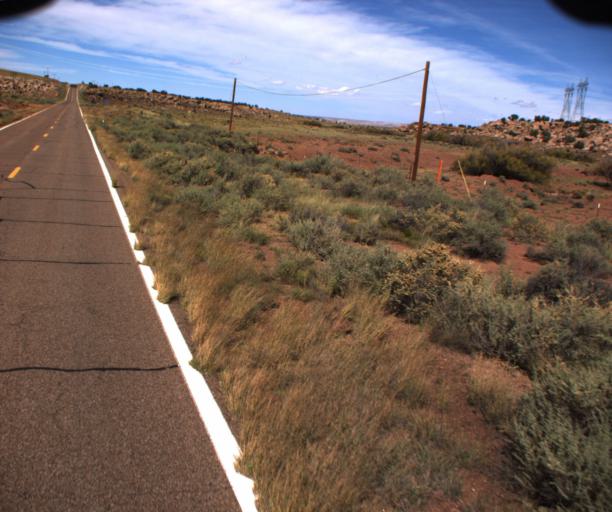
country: US
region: Arizona
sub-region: Apache County
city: Saint Johns
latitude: 34.5474
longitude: -109.6234
